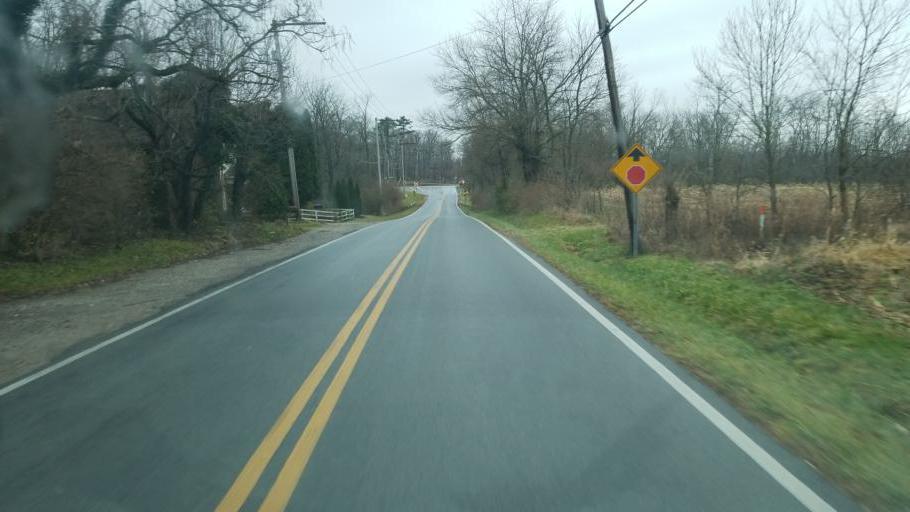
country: US
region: Ohio
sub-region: Delaware County
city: Delaware
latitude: 40.3126
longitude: -83.0526
